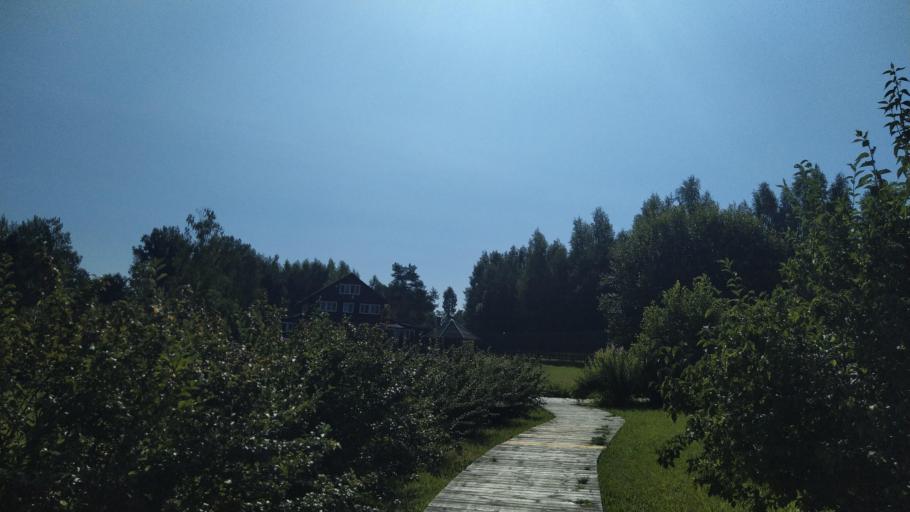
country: RU
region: Pskov
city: Pushkinskiye Gory
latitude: 56.9827
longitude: 29.0029
